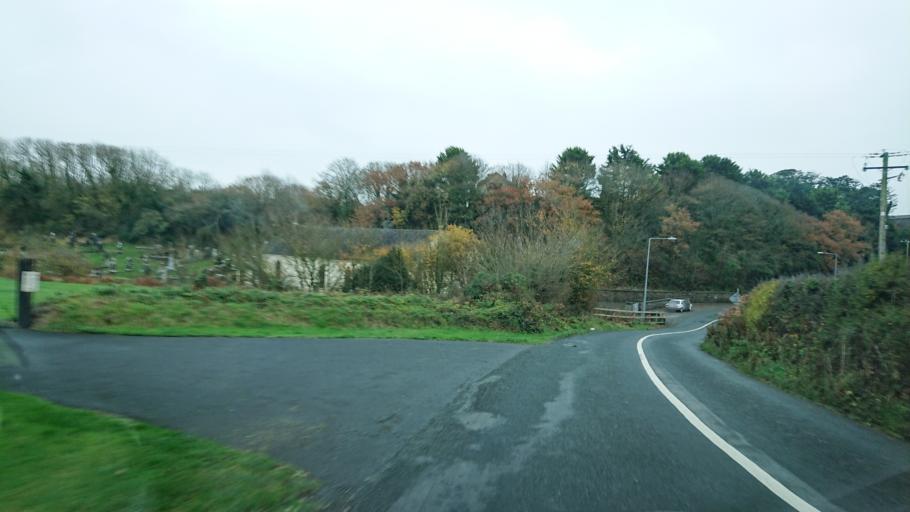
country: IE
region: Munster
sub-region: Waterford
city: Dunmore East
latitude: 52.1618
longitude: -7.0620
